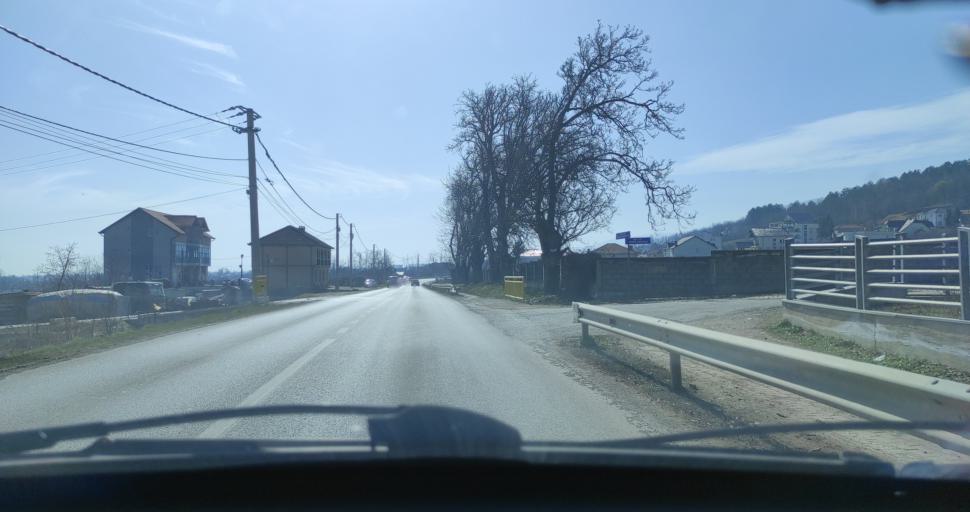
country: XK
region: Gjakova
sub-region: Komuna e Decanit
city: Lebushe
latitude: 42.5686
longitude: 20.2927
